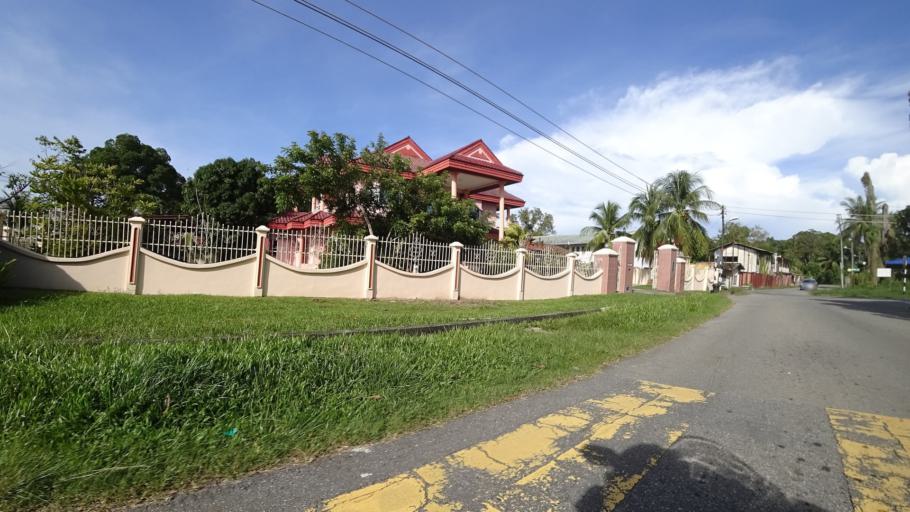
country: BN
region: Brunei and Muara
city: Bandar Seri Begawan
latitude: 4.9331
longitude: 114.8431
